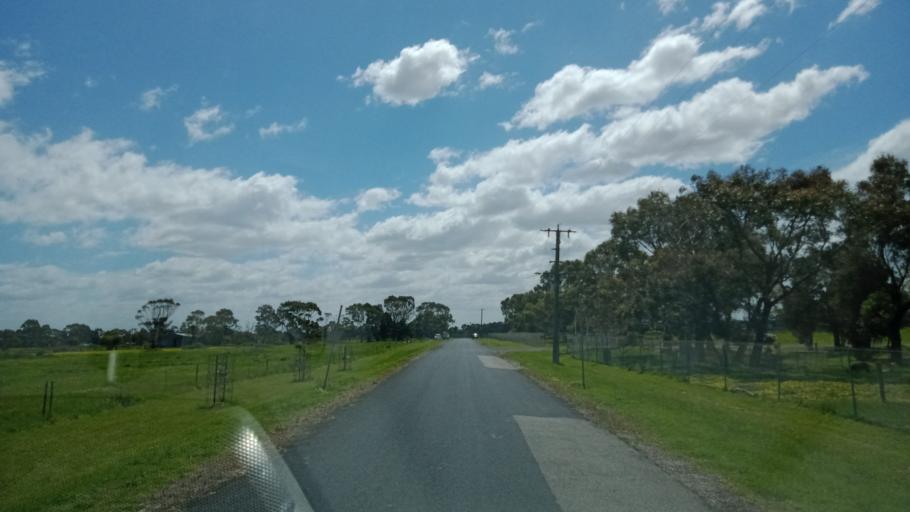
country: AU
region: Victoria
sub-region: Kingston
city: Chelsea Heights
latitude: -38.0390
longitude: 145.1442
